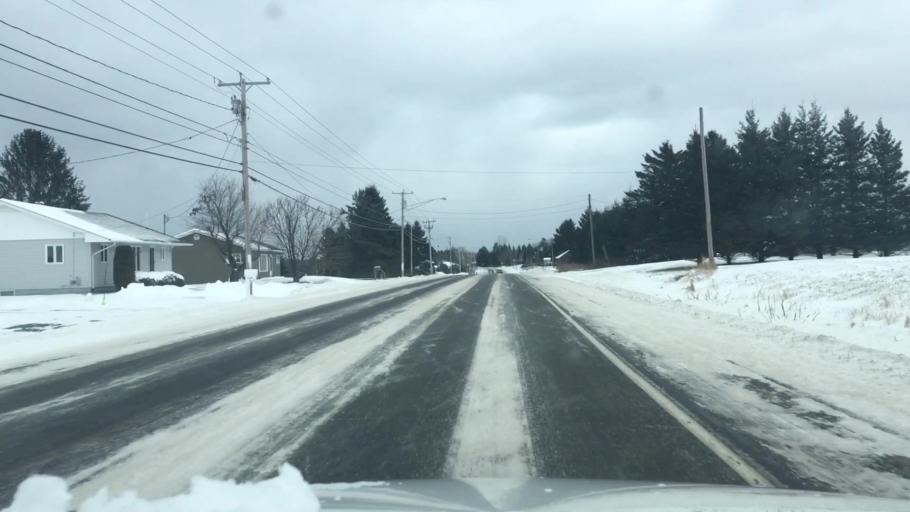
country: US
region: Maine
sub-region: Aroostook County
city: Madawaska
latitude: 47.3477
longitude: -68.2708
